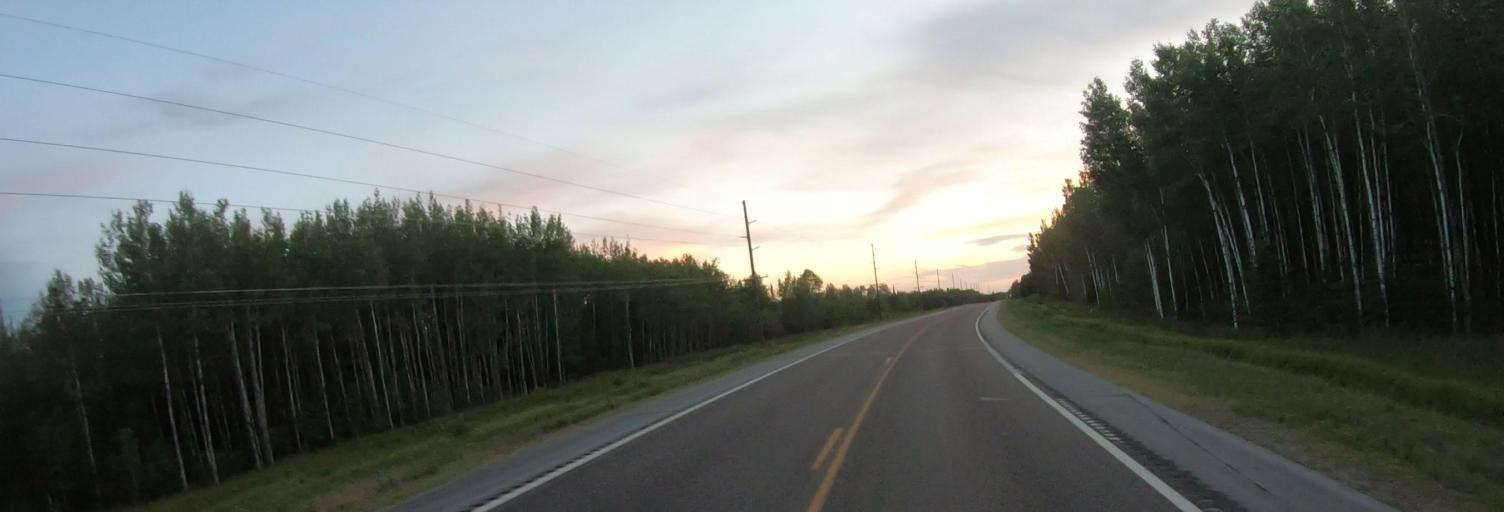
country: US
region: Minnesota
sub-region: Saint Louis County
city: Parkville
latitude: 47.8466
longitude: -92.5129
